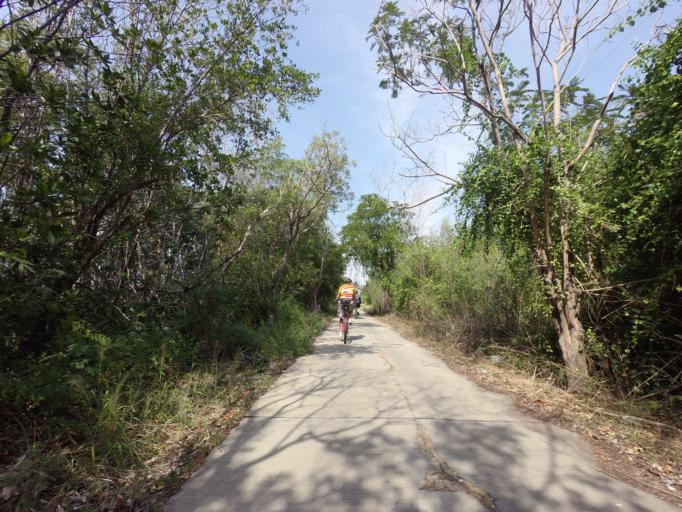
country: TH
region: Bangkok
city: Thung Khru
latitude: 13.5231
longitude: 100.4226
